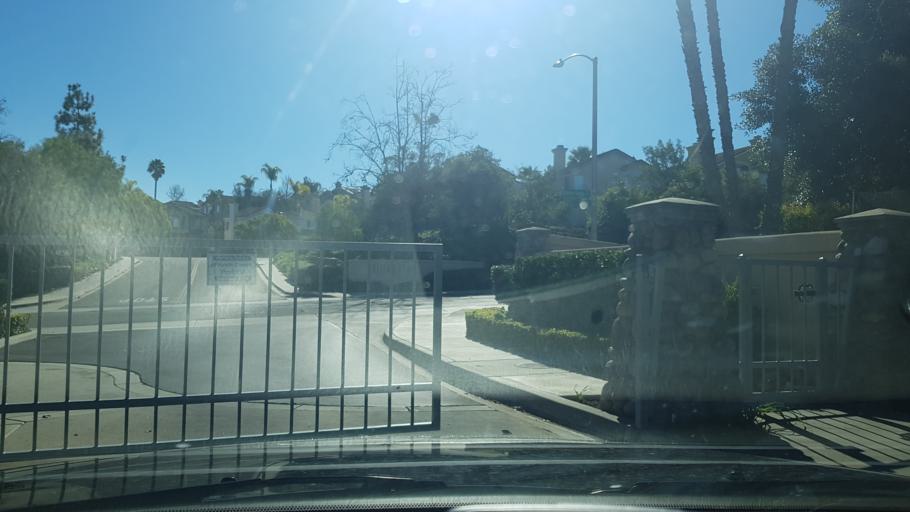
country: US
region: California
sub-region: San Diego County
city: Poway
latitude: 32.9788
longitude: -117.0693
